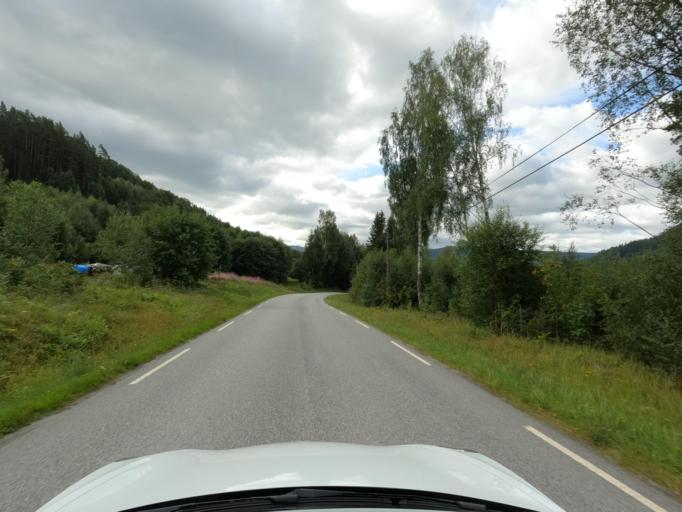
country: NO
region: Telemark
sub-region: Tinn
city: Rjukan
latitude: 60.0077
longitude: 8.8350
